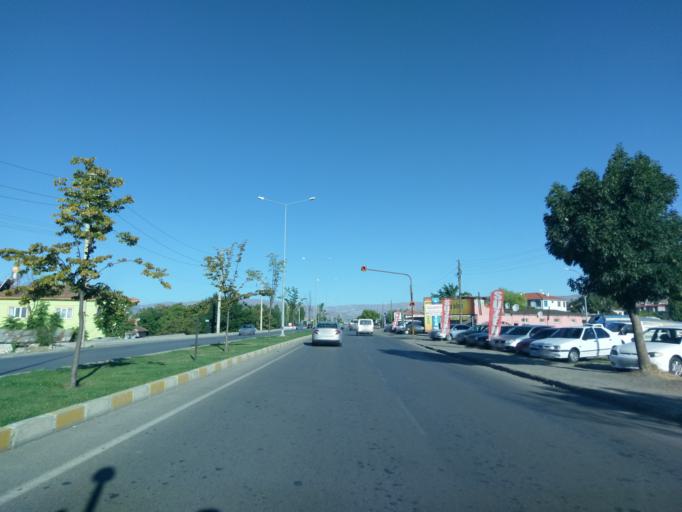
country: TR
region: Erzincan
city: Erzincan
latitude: 39.7516
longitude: 39.4567
